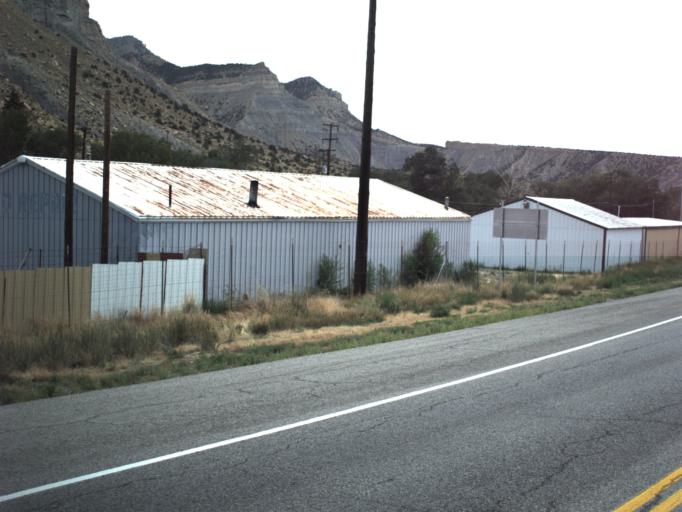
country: US
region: Utah
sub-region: Carbon County
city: Helper
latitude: 39.6949
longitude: -110.8652
